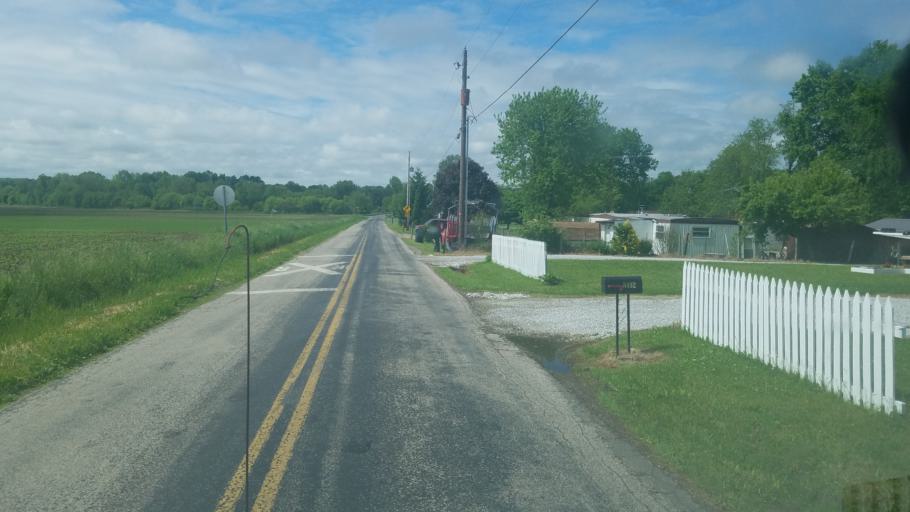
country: US
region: Ohio
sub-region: Wayne County
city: Smithville
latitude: 40.8432
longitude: -81.8220
